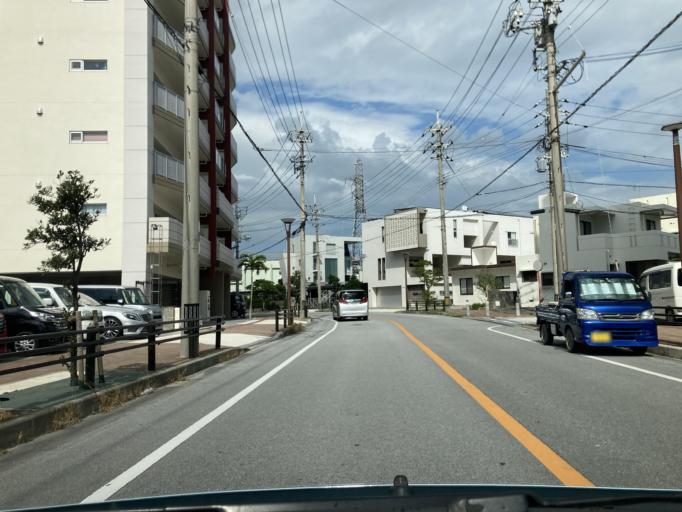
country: JP
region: Okinawa
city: Ginowan
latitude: 26.2526
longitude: 127.7755
